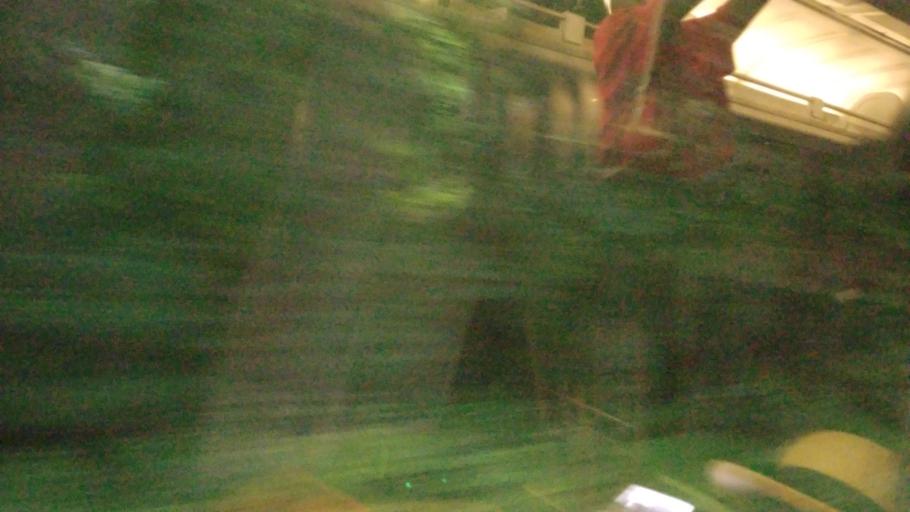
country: US
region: Virginia
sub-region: Orange County
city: Orange
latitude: 38.2945
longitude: -78.0832
